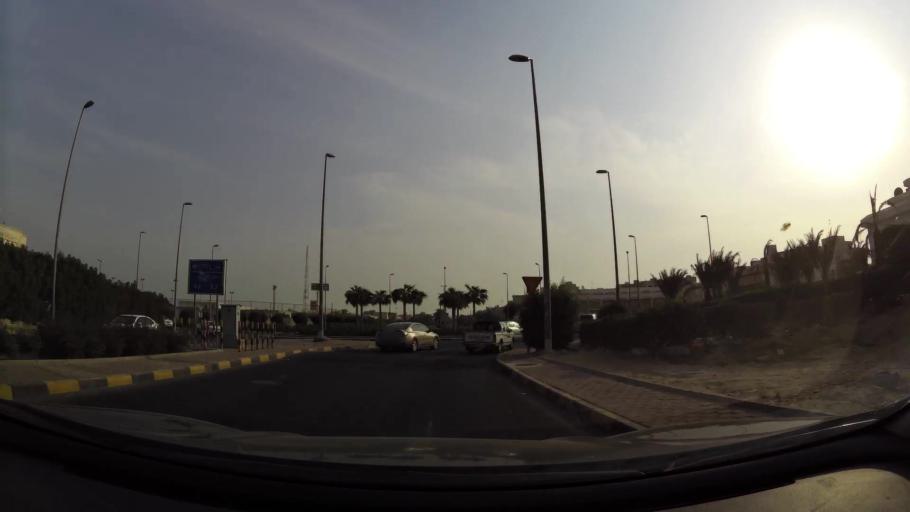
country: KW
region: Mubarak al Kabir
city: Mubarak al Kabir
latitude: 29.2043
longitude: 48.0692
